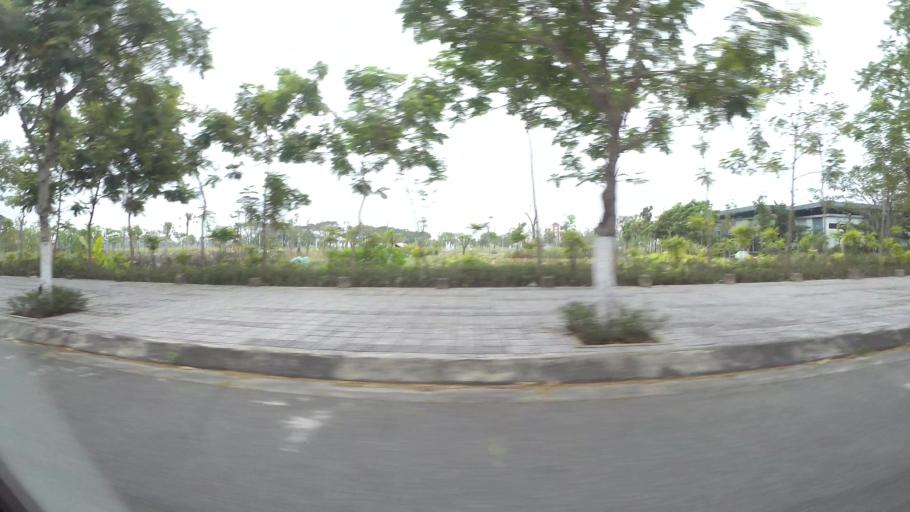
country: VN
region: Da Nang
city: Son Tra
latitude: 16.0343
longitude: 108.2323
